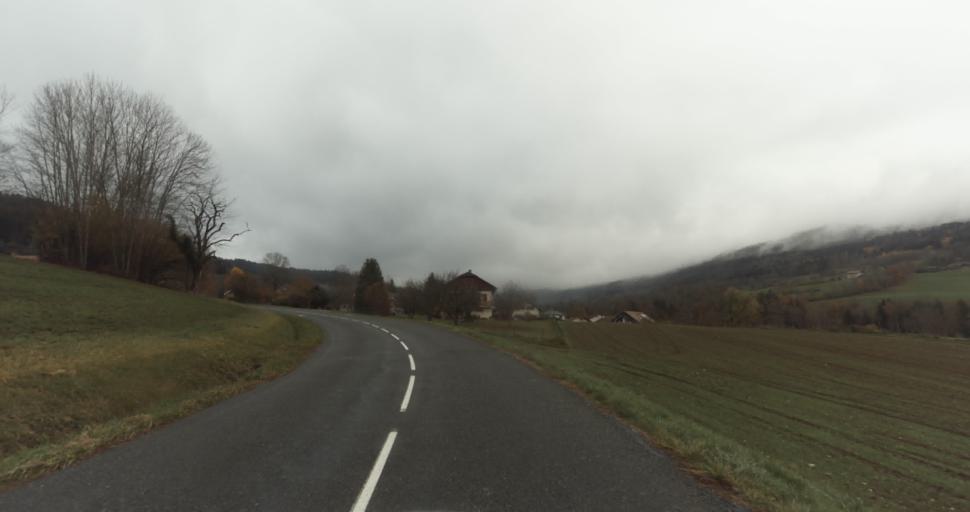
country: FR
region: Rhone-Alpes
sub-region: Departement de la Haute-Savoie
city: Thorens-Glieres
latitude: 46.0034
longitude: 6.2567
